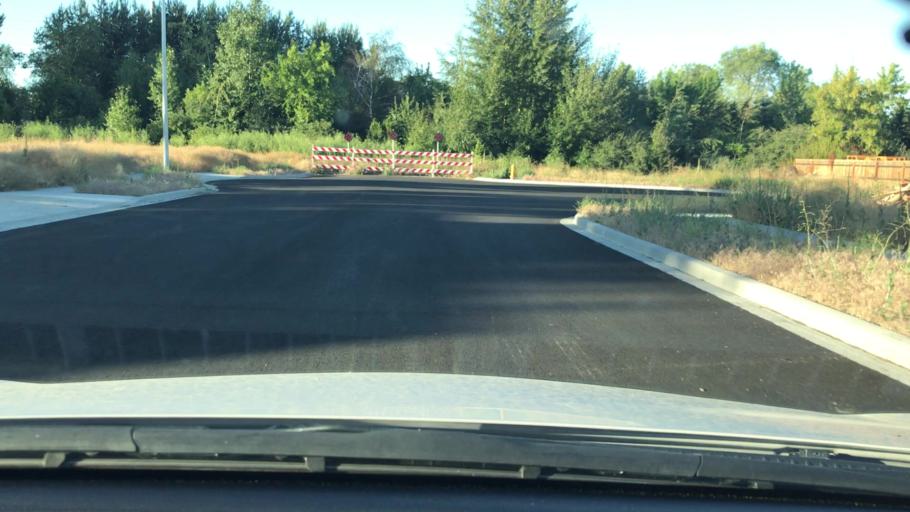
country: US
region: Washington
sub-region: Grant County
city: Moses Lake
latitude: 47.1184
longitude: -119.2524
